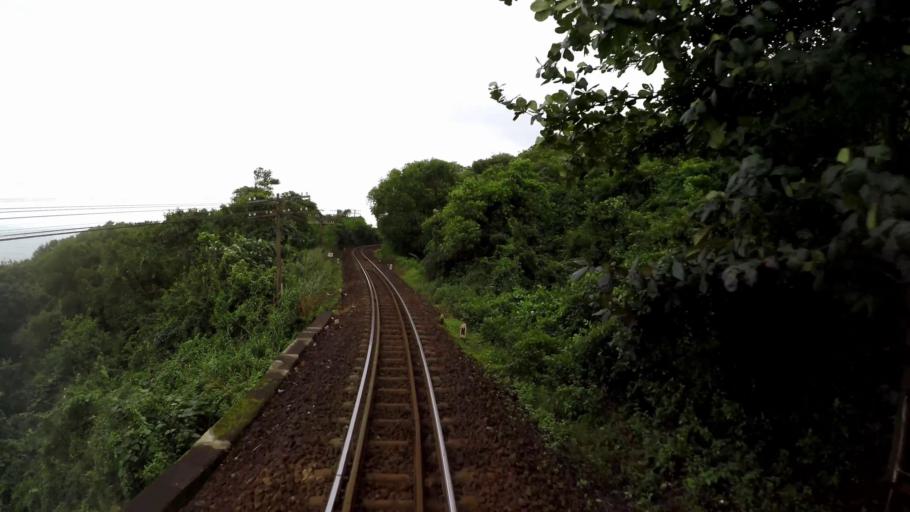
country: VN
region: Da Nang
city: Lien Chieu
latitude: 16.2145
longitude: 108.1273
